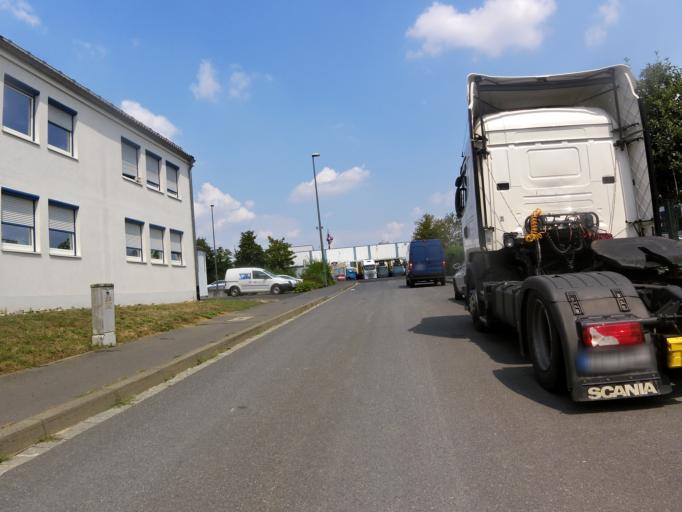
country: DE
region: Bavaria
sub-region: Regierungsbezirk Unterfranken
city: Randersacker
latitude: 49.7322
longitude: 9.9693
